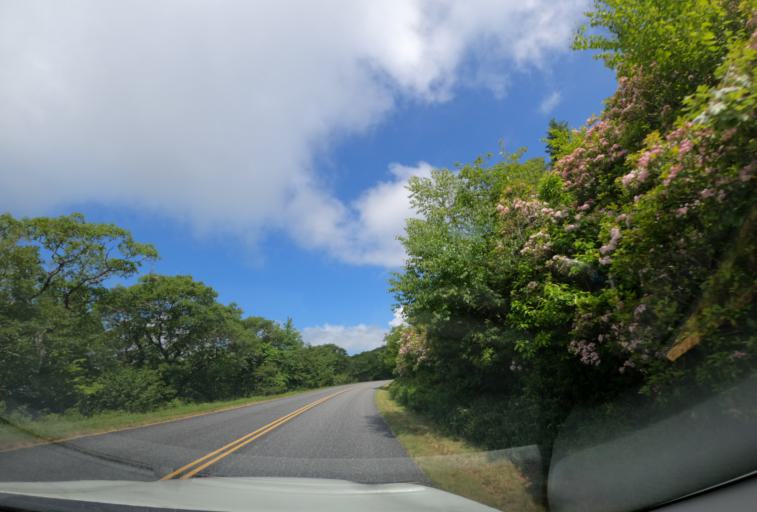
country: US
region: North Carolina
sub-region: Haywood County
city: Hazelwood
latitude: 35.3799
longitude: -83.0251
